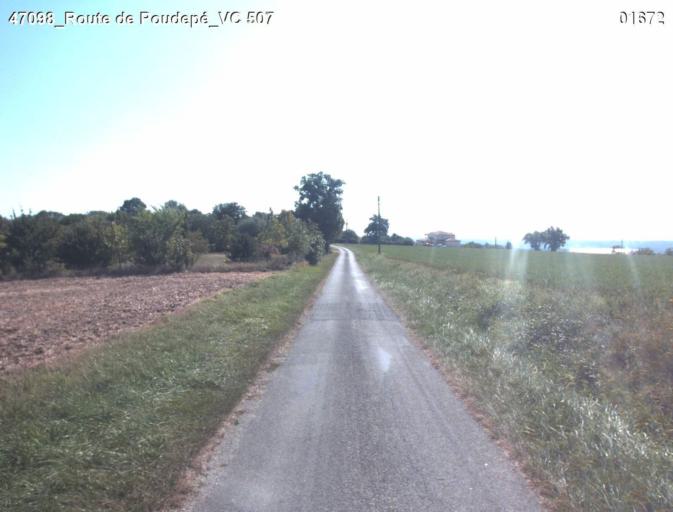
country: FR
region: Aquitaine
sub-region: Departement du Lot-et-Garonne
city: Nerac
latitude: 44.1051
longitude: 0.4025
